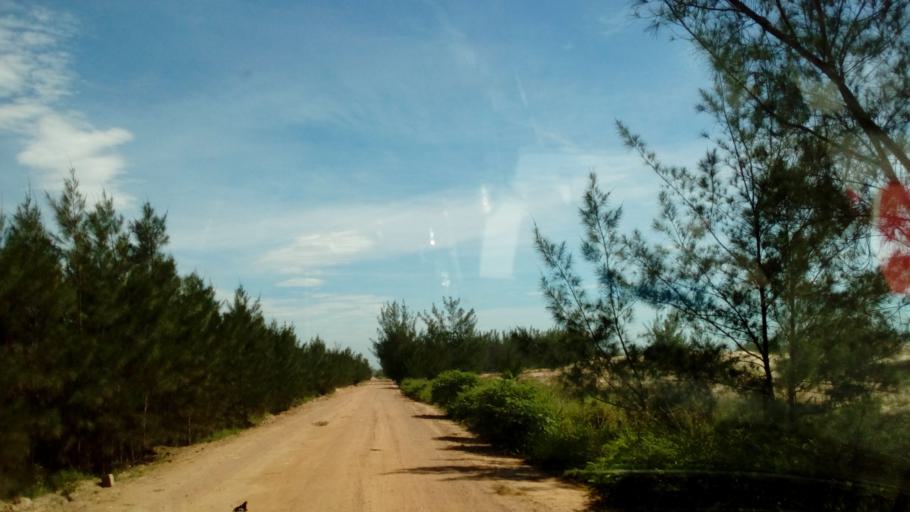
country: BR
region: Santa Catarina
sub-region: Laguna
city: Laguna
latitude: -28.4521
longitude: -48.7645
